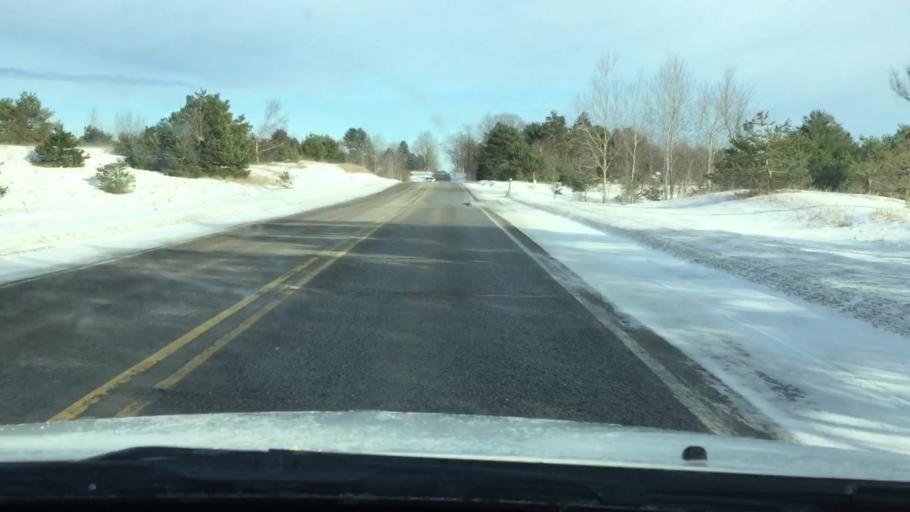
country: US
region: Michigan
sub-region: Kalkaska County
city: Kalkaska
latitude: 44.6405
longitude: -85.1942
